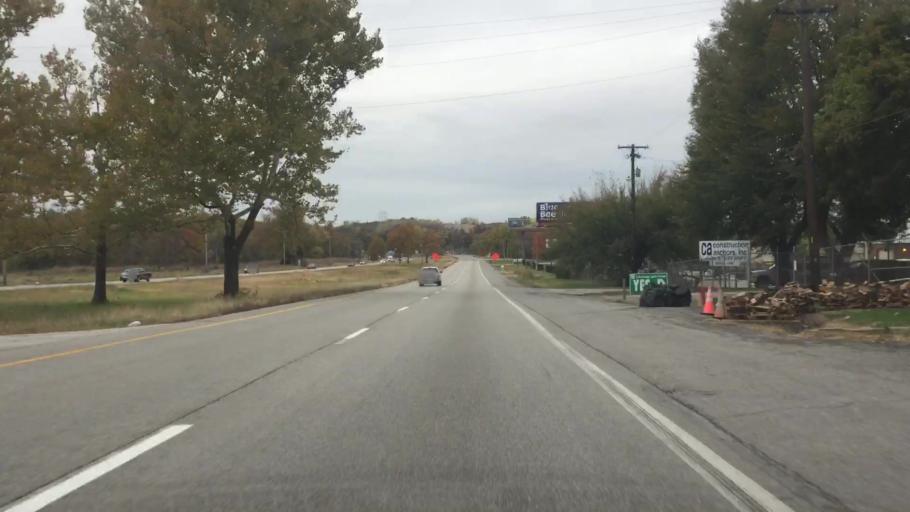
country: US
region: Missouri
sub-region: Jackson County
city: Raytown
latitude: 38.9600
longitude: -94.4232
